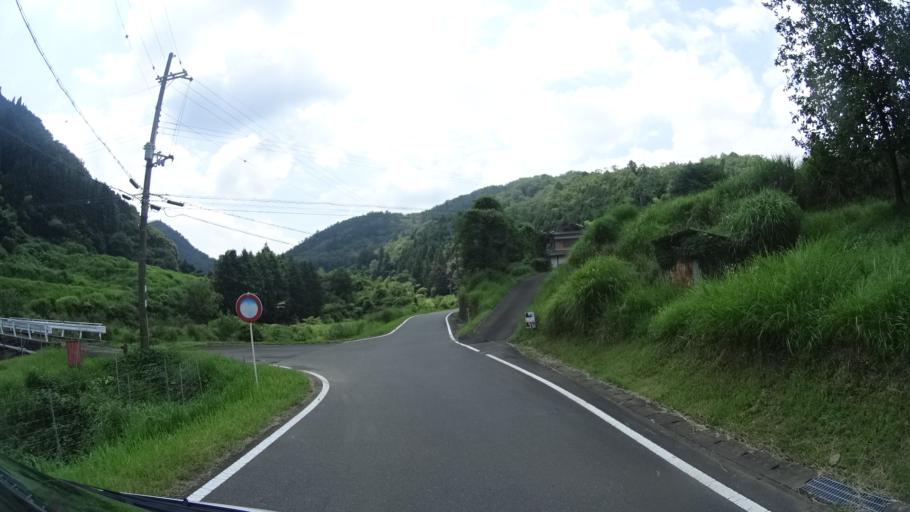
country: JP
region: Kyoto
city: Ayabe
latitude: 35.1917
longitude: 135.2169
